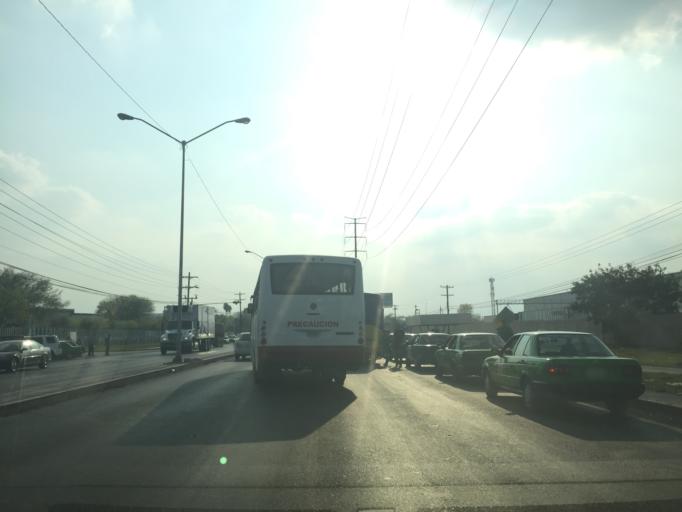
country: MX
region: Nuevo Leon
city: Apodaca
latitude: 25.7644
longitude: -100.2035
